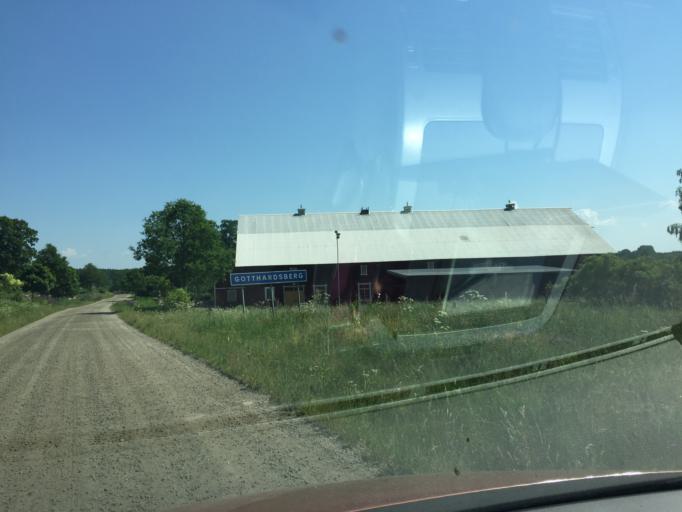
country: SE
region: Soedermanland
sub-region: Flens Kommun
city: Flen
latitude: 58.9304
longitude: 16.4658
